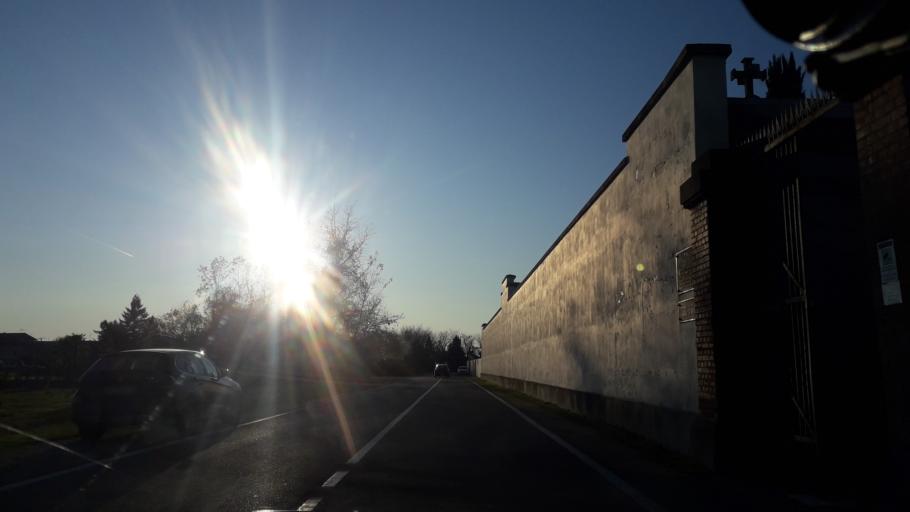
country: IT
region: Friuli Venezia Giulia
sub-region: Provincia di Udine
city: Passons
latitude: 46.0608
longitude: 13.2158
